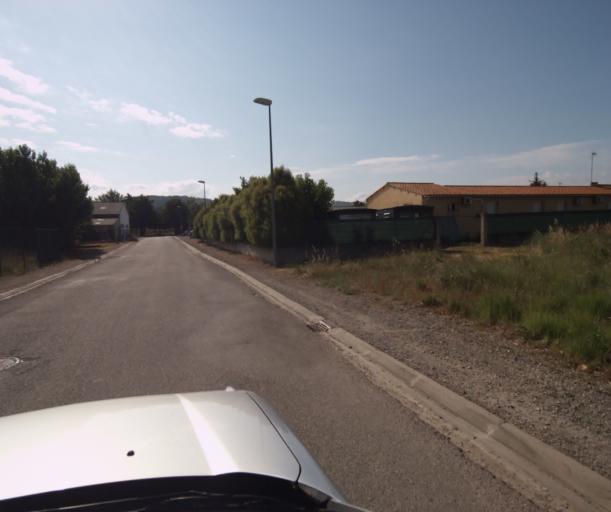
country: FR
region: Languedoc-Roussillon
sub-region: Departement de l'Aude
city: Limoux
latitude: 43.0757
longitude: 2.2201
